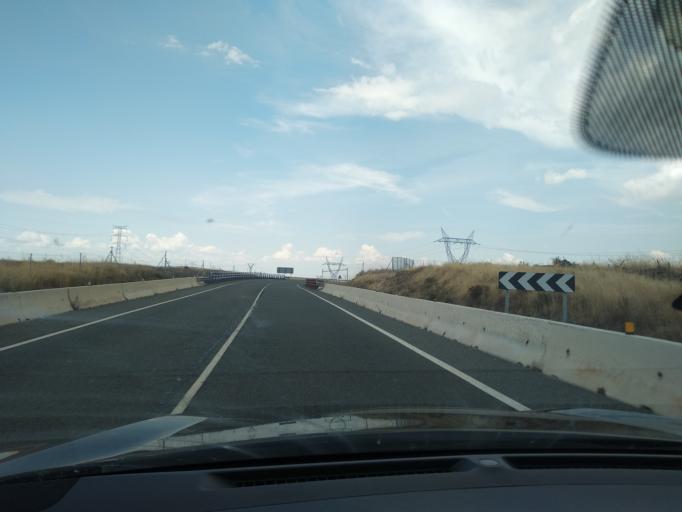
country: ES
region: Castille and Leon
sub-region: Provincia de Segovia
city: Otero de Herreros
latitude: 40.8019
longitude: -4.2104
